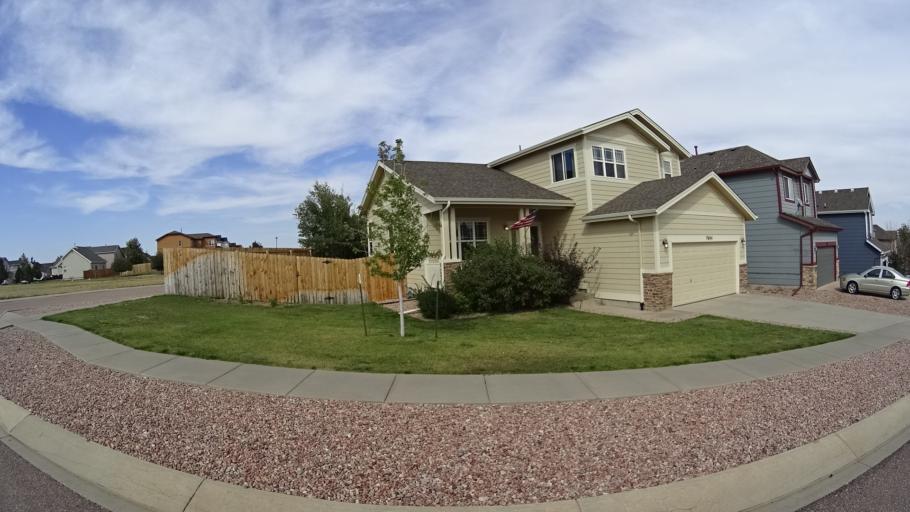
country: US
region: Colorado
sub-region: El Paso County
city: Cimarron Hills
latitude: 38.9059
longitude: -104.6870
